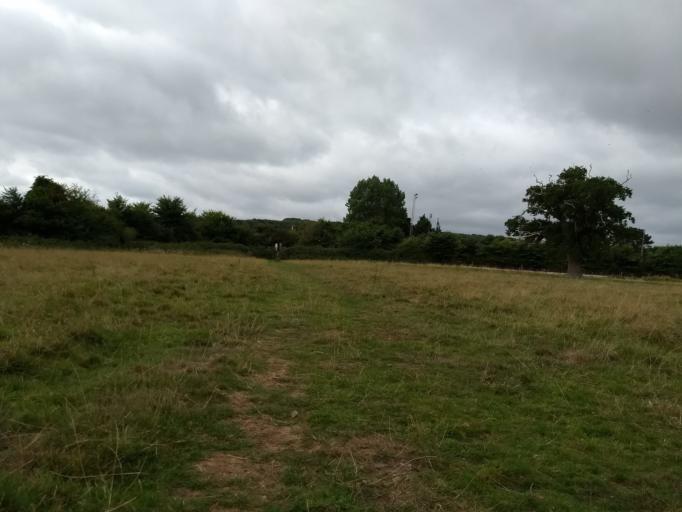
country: GB
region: England
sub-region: Isle of Wight
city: Brading
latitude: 50.6850
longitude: -1.1377
